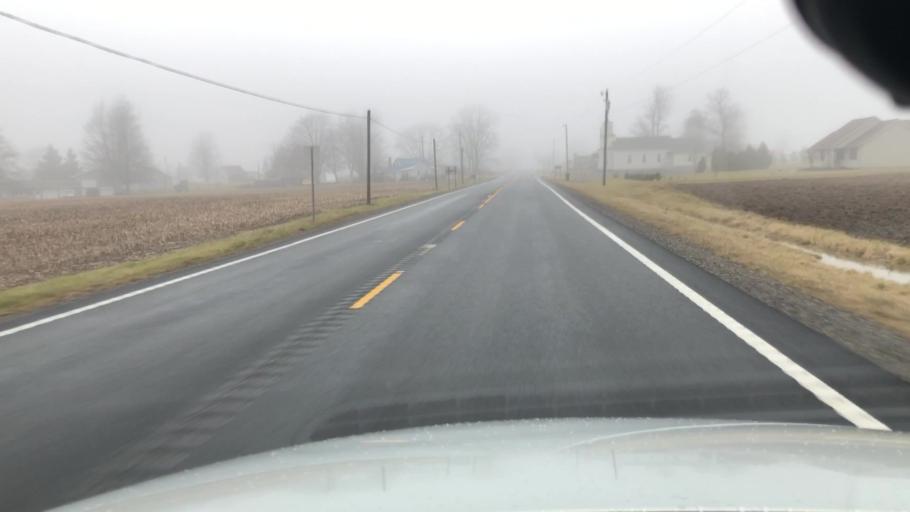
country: US
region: Ohio
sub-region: Logan County
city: Lakeview
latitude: 40.6016
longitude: -83.8785
